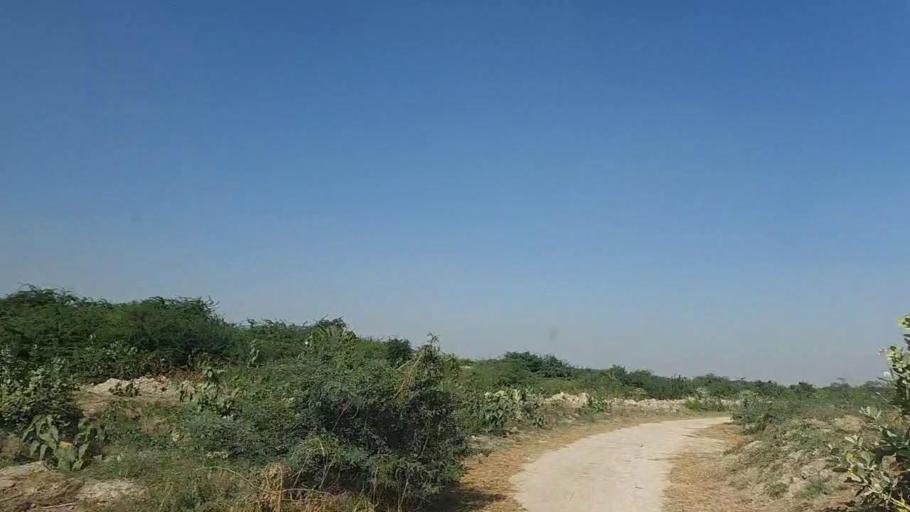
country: PK
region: Sindh
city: Daro Mehar
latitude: 24.7644
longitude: 68.1550
